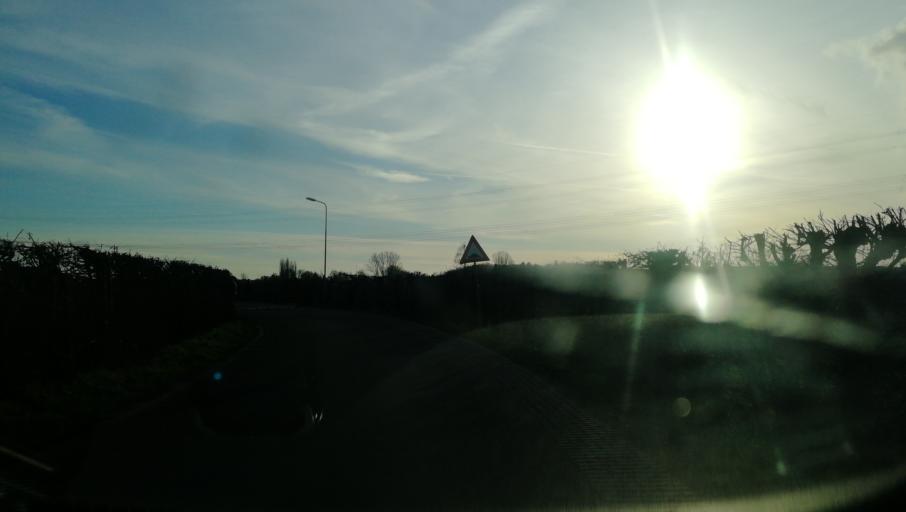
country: NL
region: Limburg
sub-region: Gemeente Venlo
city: Tegelen
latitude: 51.3386
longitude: 6.1063
